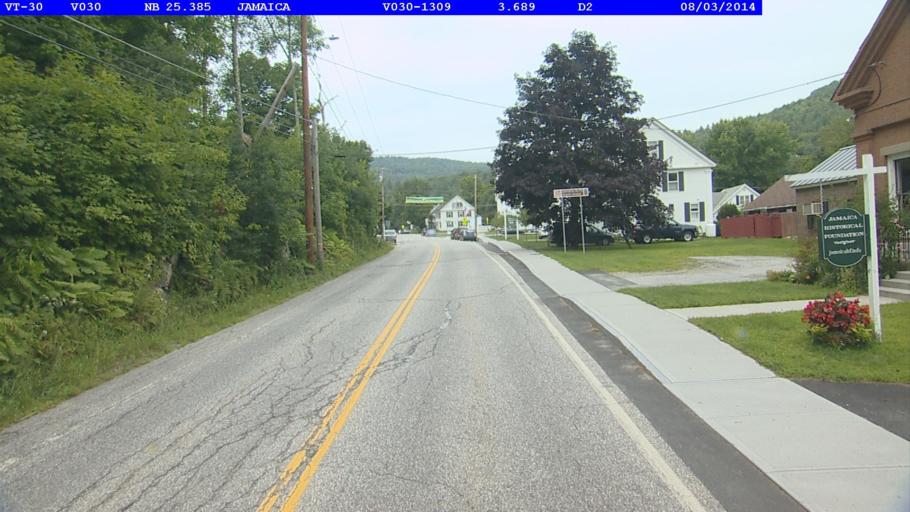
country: US
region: Vermont
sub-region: Windham County
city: Dover
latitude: 43.1001
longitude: -72.7768
